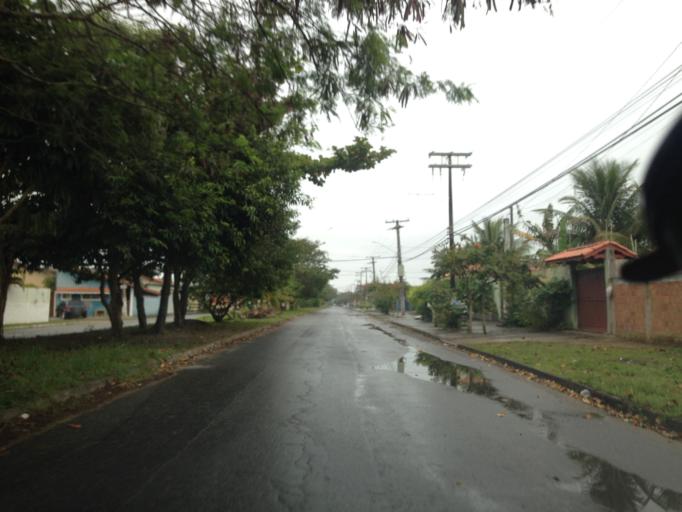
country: BR
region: Sao Paulo
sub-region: Itanhaem
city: Itanhaem
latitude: -24.2261
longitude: -46.8676
